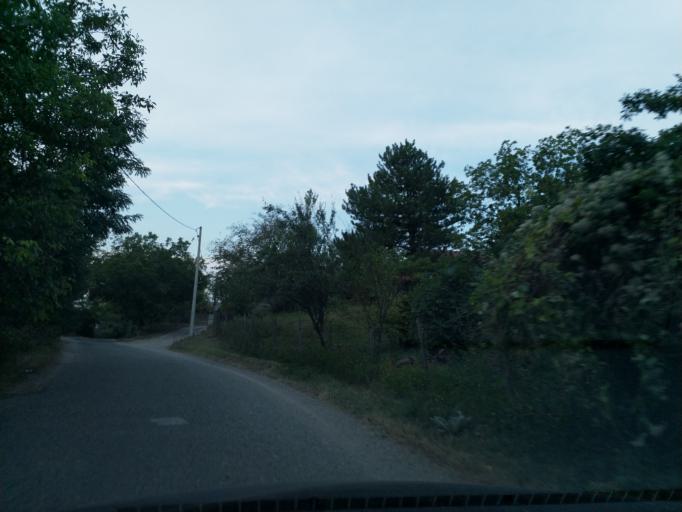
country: RS
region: Central Serbia
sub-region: Pomoravski Okrug
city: Paracin
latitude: 43.8486
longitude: 21.5281
